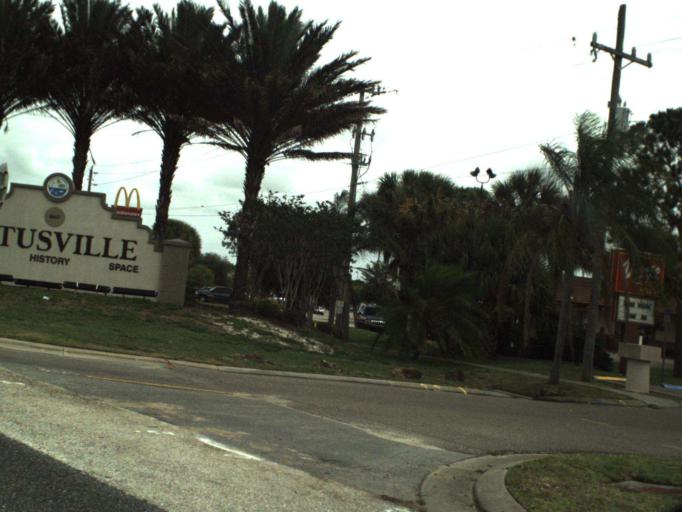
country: US
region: Florida
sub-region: Brevard County
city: Titusville
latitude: 28.5530
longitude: -80.8481
